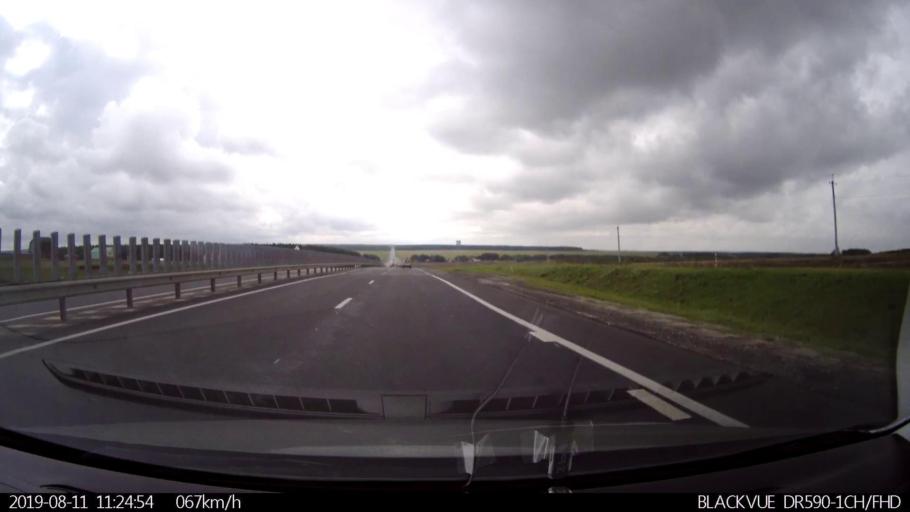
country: RU
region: Ulyanovsk
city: Krasnyy Gulyay
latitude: 54.1232
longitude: 48.2400
